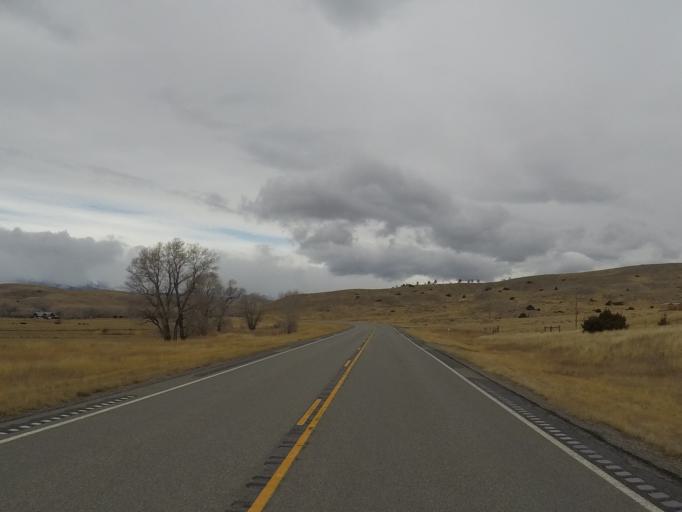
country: US
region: Montana
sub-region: Sweet Grass County
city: Big Timber
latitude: 45.8977
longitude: -109.9651
